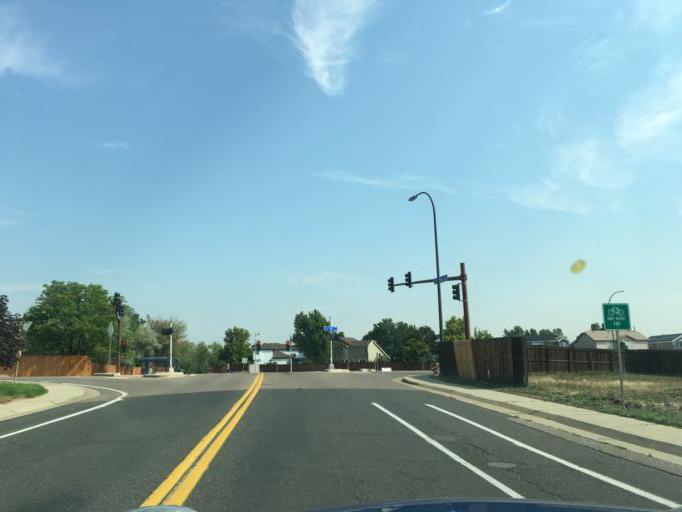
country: US
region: Colorado
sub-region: Adams County
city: Westminster
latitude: 39.8407
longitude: -105.0625
